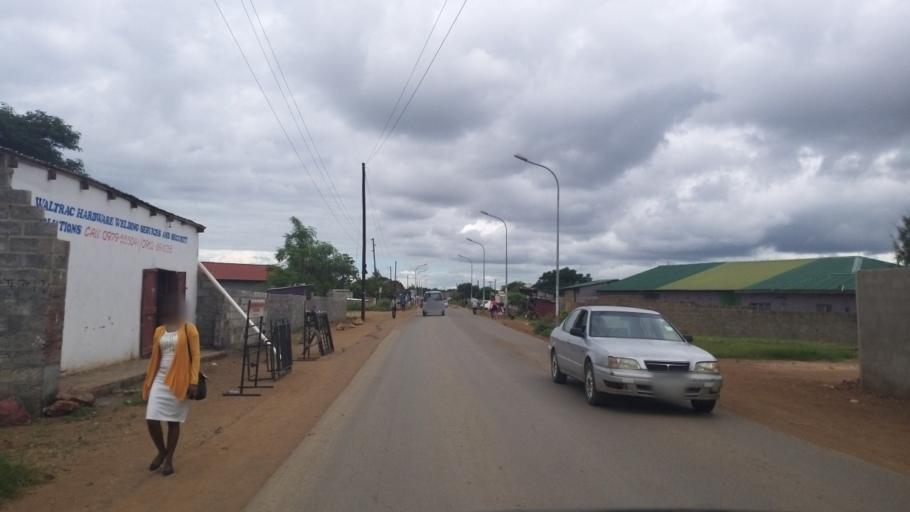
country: ZM
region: Lusaka
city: Lusaka
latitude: -15.4442
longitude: 28.3067
